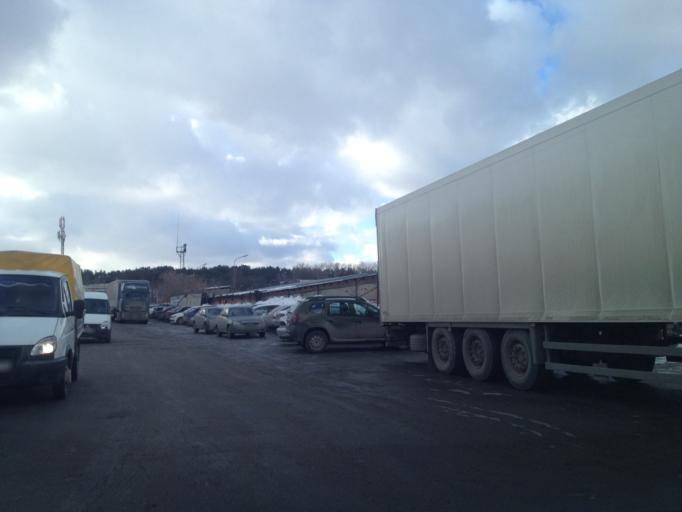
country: RU
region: Sverdlovsk
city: Yekaterinburg
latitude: 56.7868
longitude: 60.6107
